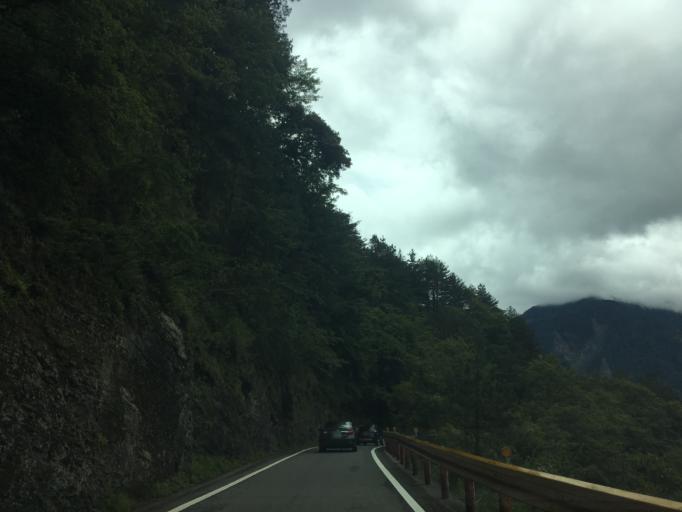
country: TW
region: Taiwan
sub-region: Hualien
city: Hualian
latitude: 24.1891
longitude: 121.3342
